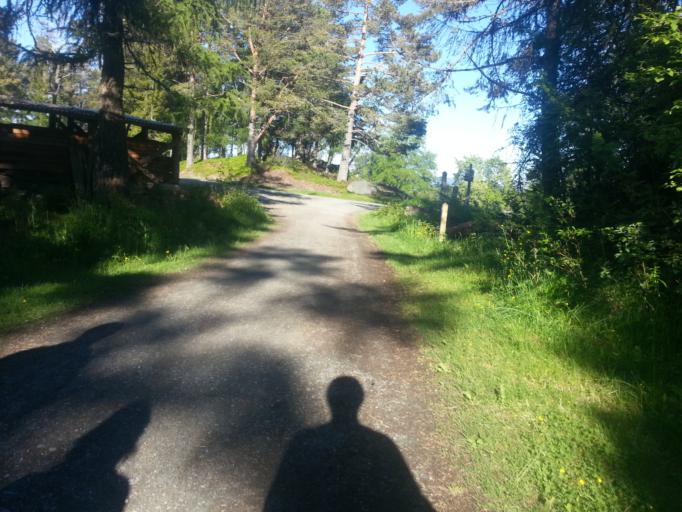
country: NO
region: Sor-Trondelag
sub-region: Trondheim
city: Trondheim
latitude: 63.4216
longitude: 10.3323
